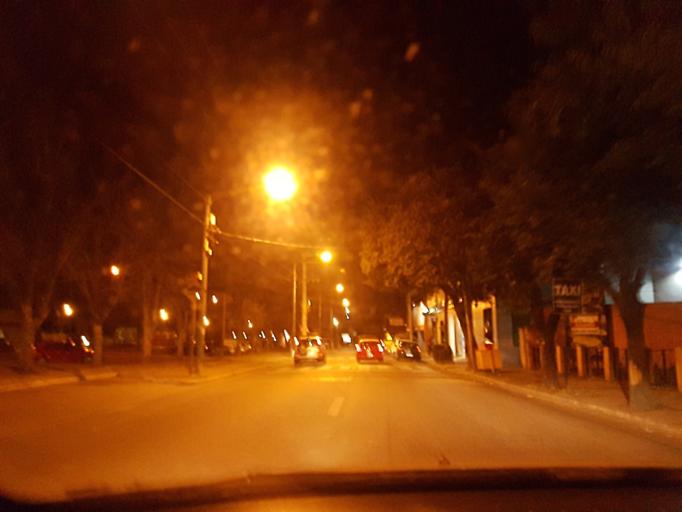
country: AR
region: Cordoba
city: Villa Allende
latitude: -31.2908
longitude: -64.2929
